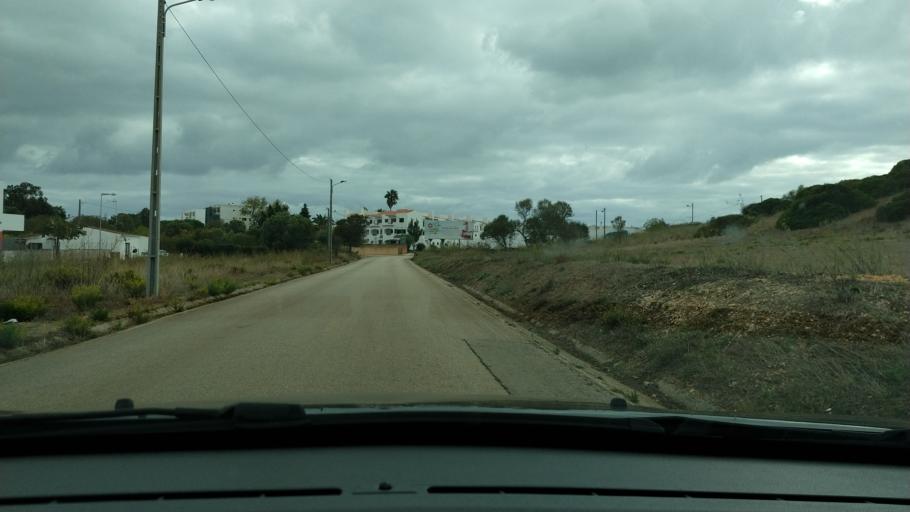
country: PT
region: Faro
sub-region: Lagos
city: Lagos
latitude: 37.0769
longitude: -8.7757
